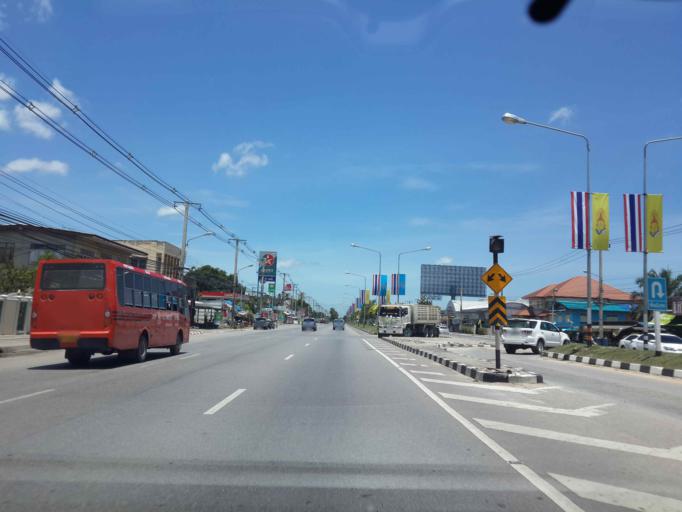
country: TH
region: Phetchaburi
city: Cha-am
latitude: 12.8414
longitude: 99.9300
